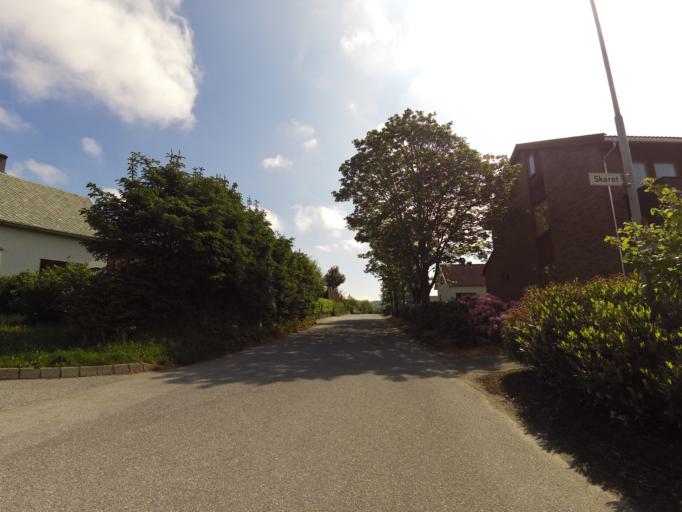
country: NO
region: Rogaland
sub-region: Ha
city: Vigrestad
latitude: 58.5202
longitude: 5.8073
